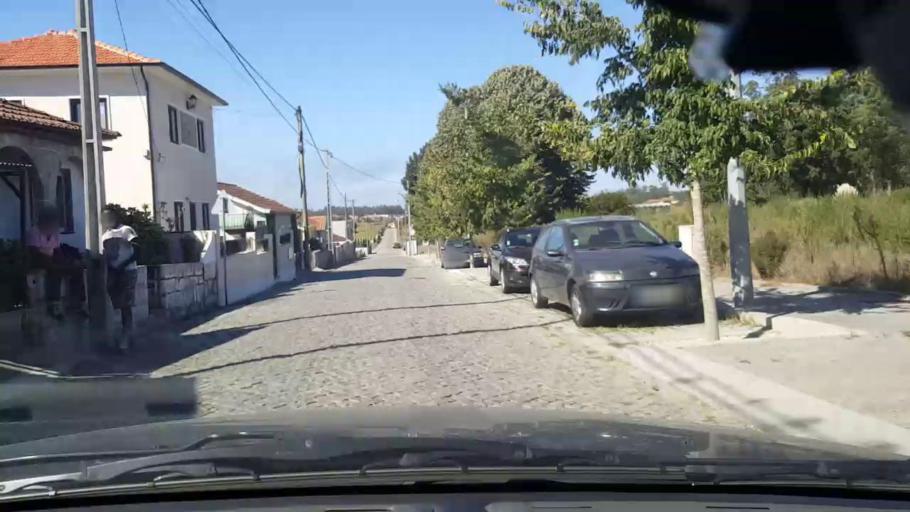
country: PT
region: Porto
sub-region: Maia
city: Gemunde
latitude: 41.2803
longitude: -8.6630
